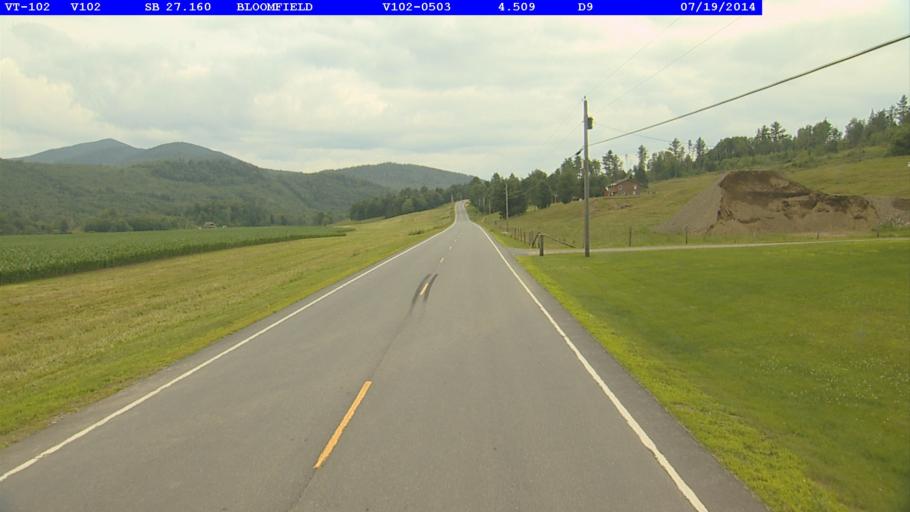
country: US
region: New Hampshire
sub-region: Coos County
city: Colebrook
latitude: 44.7960
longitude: -71.5764
